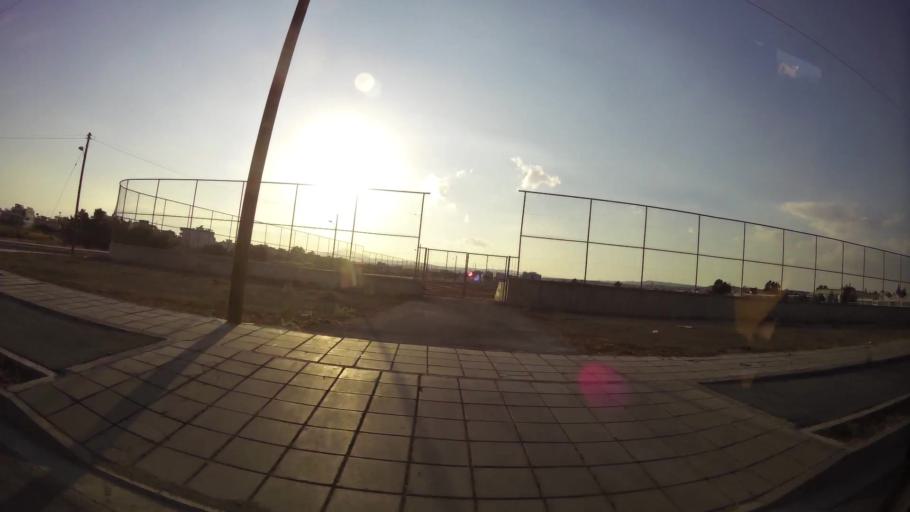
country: CY
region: Larnaka
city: Larnaca
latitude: 34.9180
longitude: 33.5971
